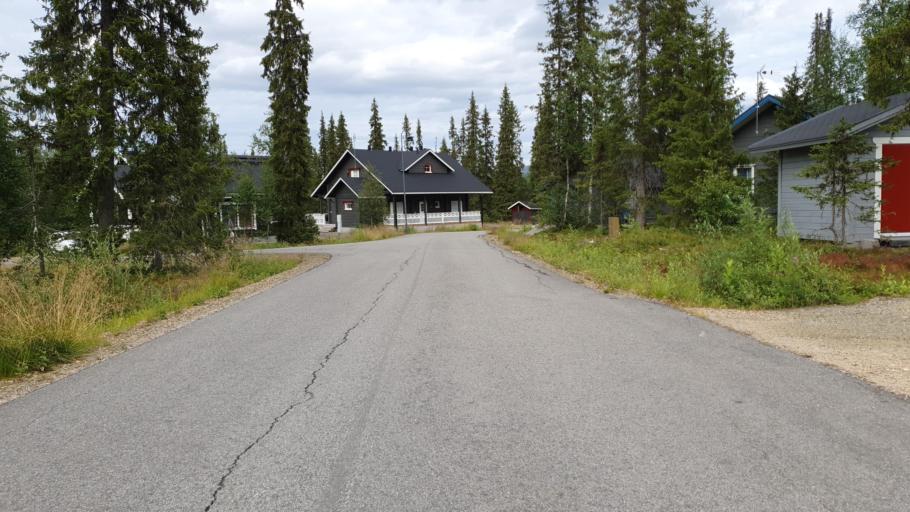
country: FI
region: Lapland
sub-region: Tunturi-Lappi
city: Kolari
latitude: 67.6016
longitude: 24.1432
